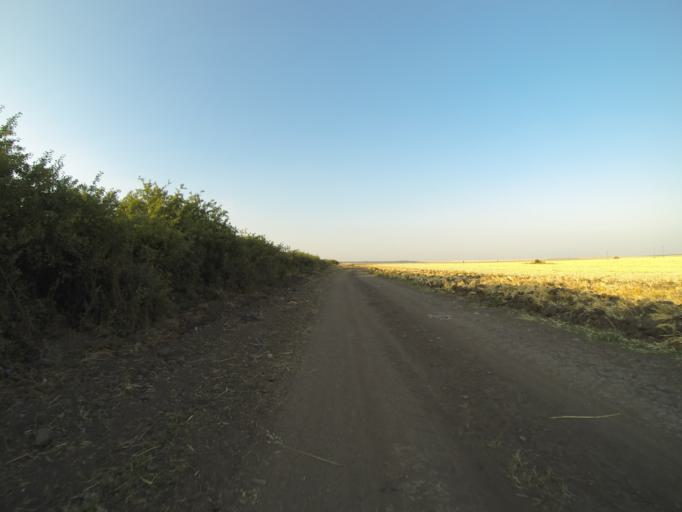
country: RO
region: Dolj
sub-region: Comuna Ceratu
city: Ceratu
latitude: 44.0655
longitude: 23.6960
